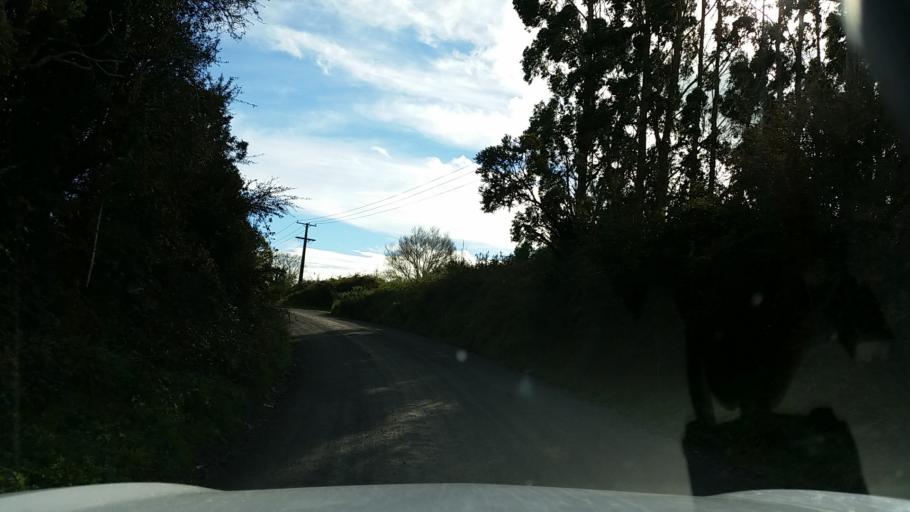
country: NZ
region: Bay of Plenty
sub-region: Rotorua District
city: Rotorua
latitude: -38.0629
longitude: 176.2091
